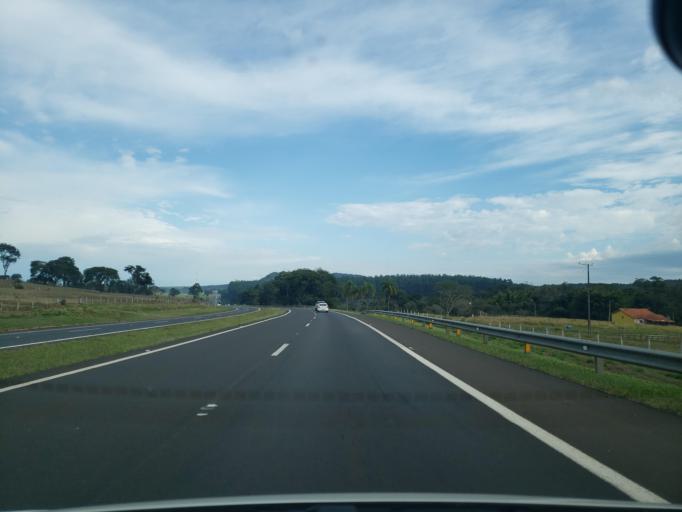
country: BR
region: Sao Paulo
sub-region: Itirapina
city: Itirapina
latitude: -22.2737
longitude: -47.9548
